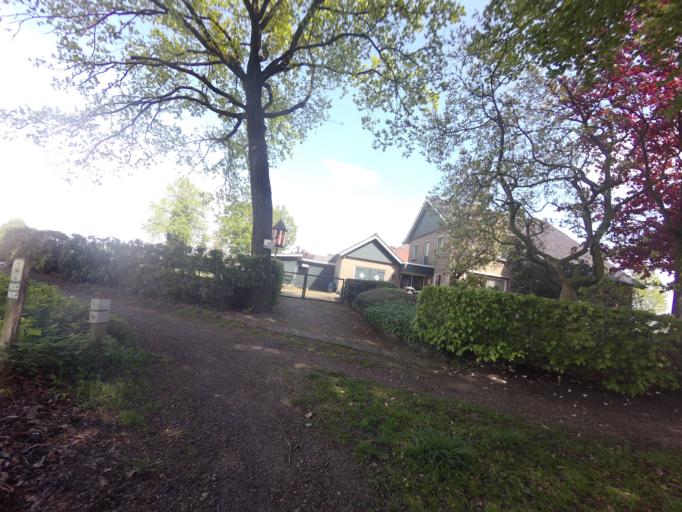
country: NL
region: Overijssel
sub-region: Gemeente Haaksbergen
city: Haaksbergen
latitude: 52.1543
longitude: 6.7546
